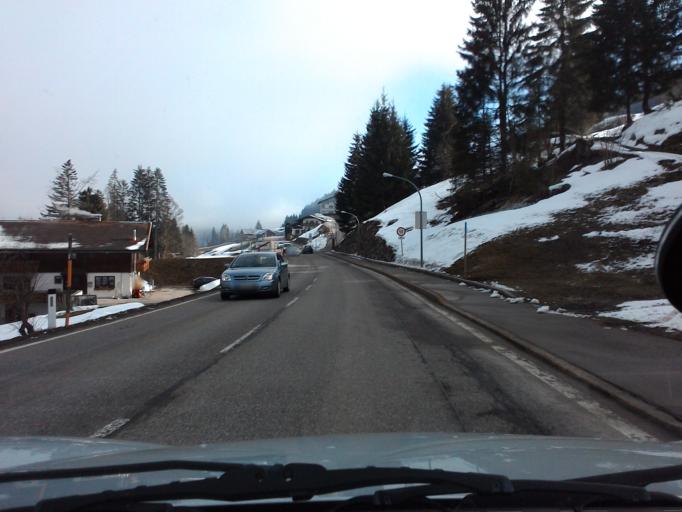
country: AT
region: Vorarlberg
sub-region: Politischer Bezirk Bregenz
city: Mittelberg
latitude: 47.3677
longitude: 10.2007
